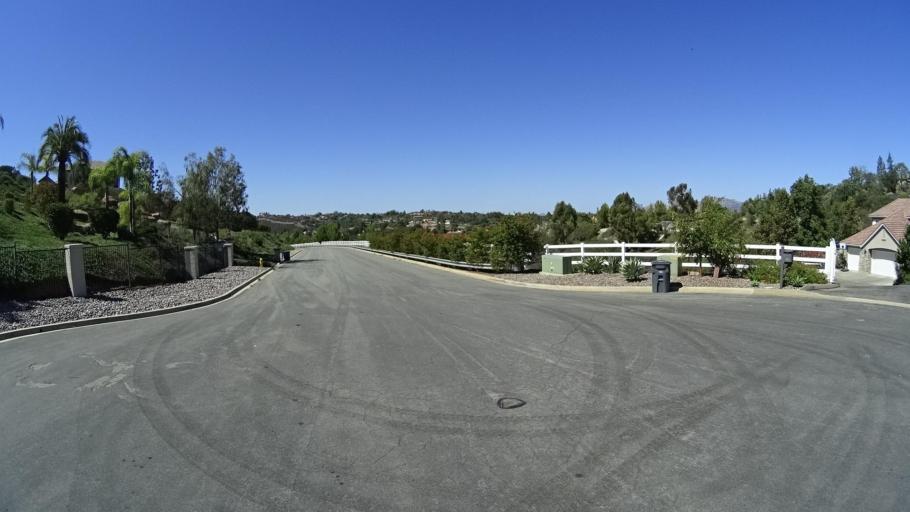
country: US
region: California
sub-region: San Diego County
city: Alpine
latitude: 32.8088
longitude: -116.7728
